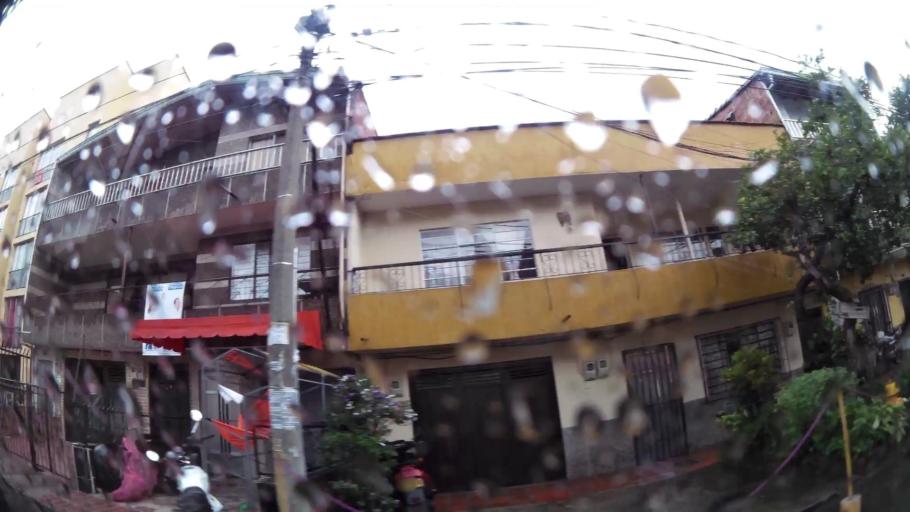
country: CO
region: Antioquia
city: Itagui
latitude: 6.1801
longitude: -75.5996
